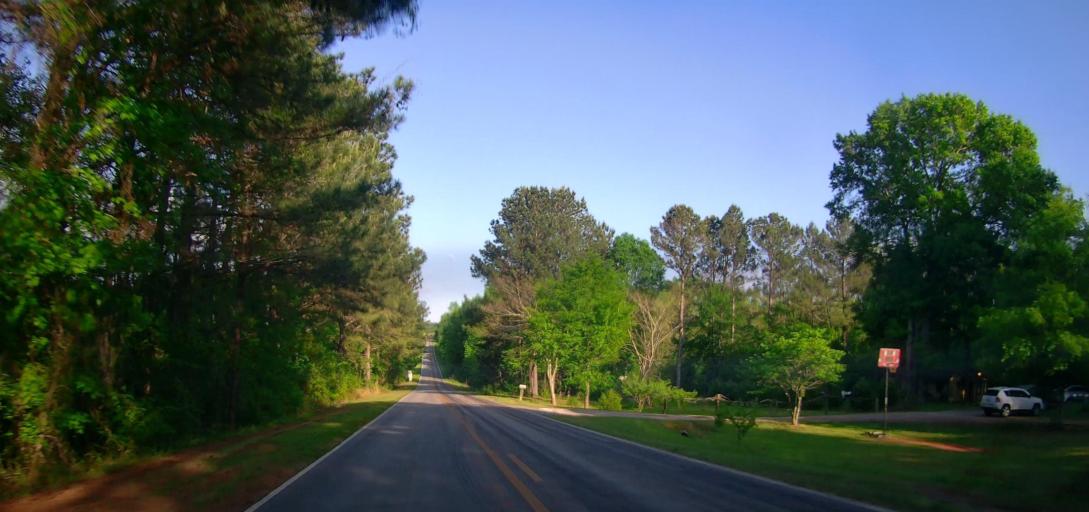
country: US
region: Georgia
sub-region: Putnam County
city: Eatonton
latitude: 33.3089
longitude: -83.3538
